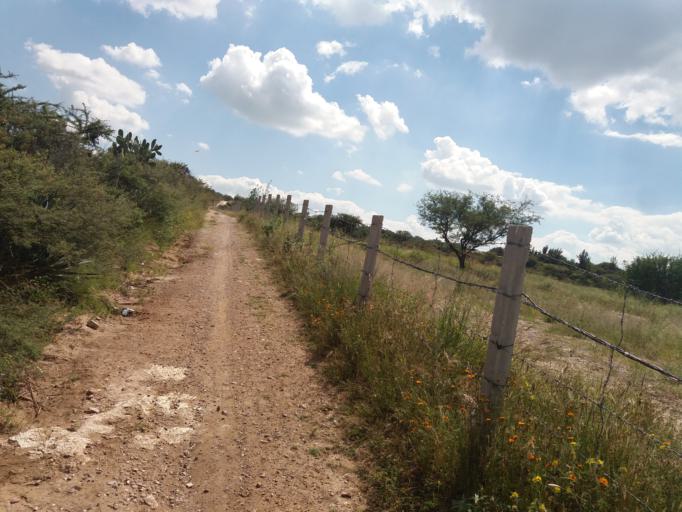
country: MX
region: Aguascalientes
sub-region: Aguascalientes
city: San Sebastian [Fraccionamiento]
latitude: 21.8011
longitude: -102.2426
